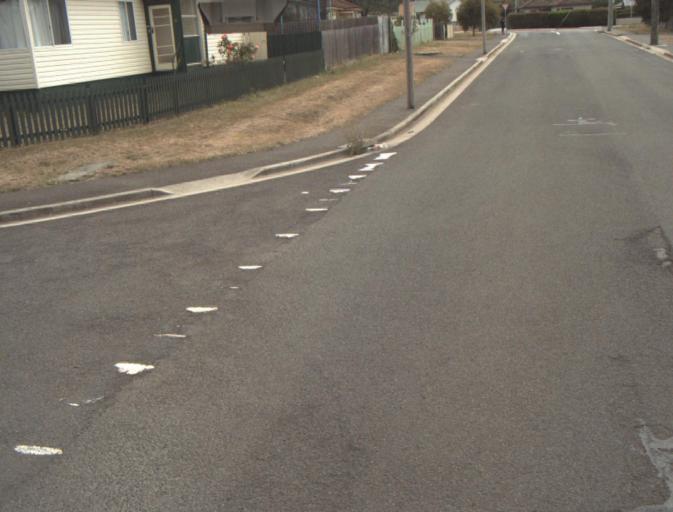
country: AU
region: Tasmania
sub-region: Launceston
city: Mayfield
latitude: -41.3889
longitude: 147.1320
